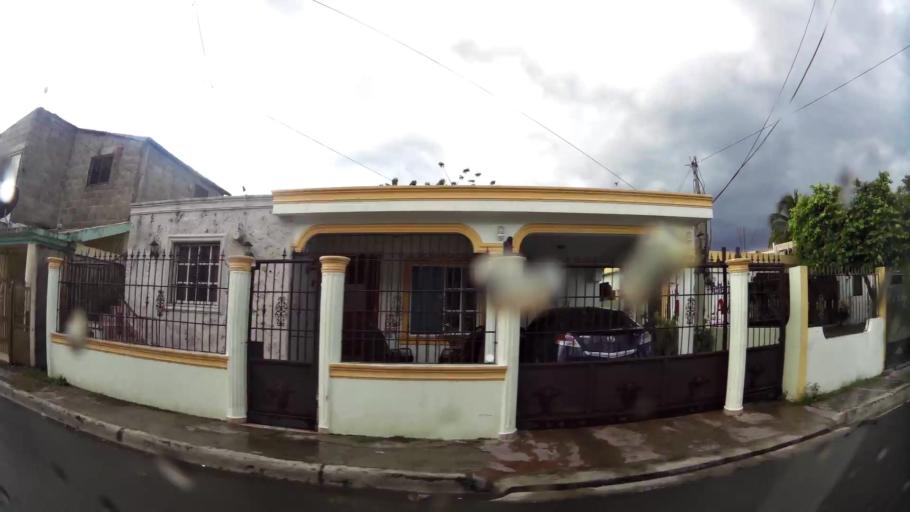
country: DO
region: Monsenor Nouel
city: Bonao
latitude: 18.9328
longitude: -70.3984
